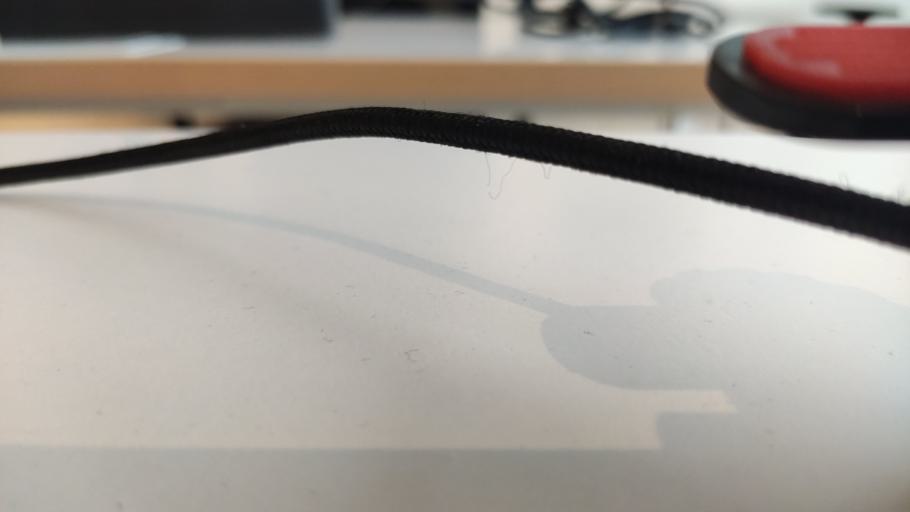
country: RU
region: Moskovskaya
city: Klin
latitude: 56.3273
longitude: 36.7024
